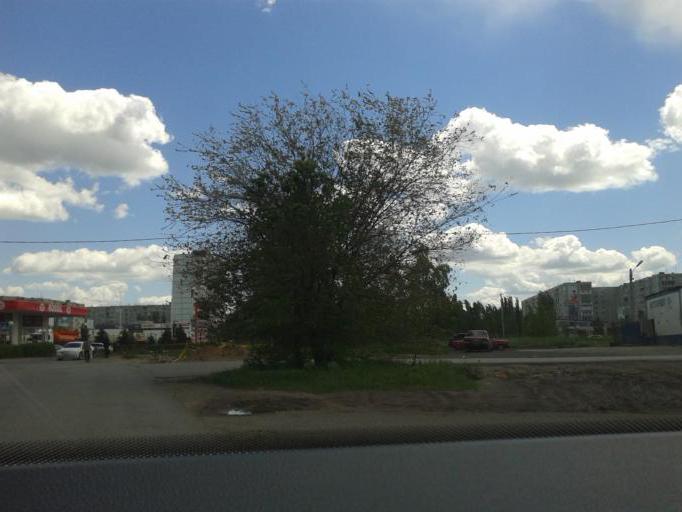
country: RU
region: Volgograd
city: Volgograd
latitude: 48.7605
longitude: 44.4988
